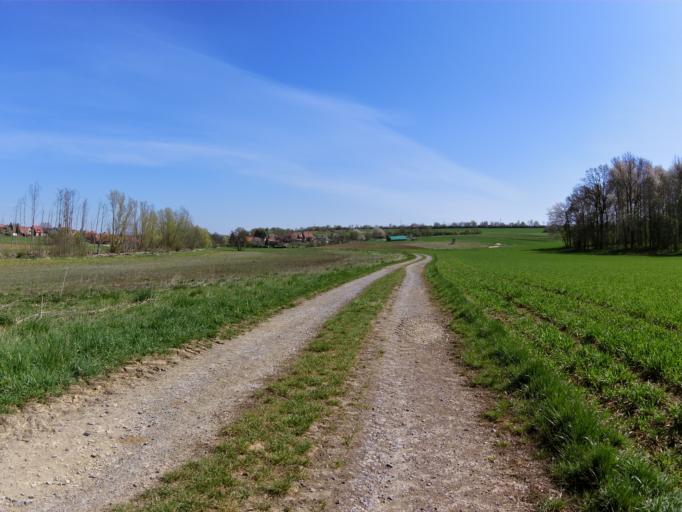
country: DE
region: Bavaria
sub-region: Regierungsbezirk Unterfranken
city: Estenfeld
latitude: 49.8555
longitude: 10.0042
